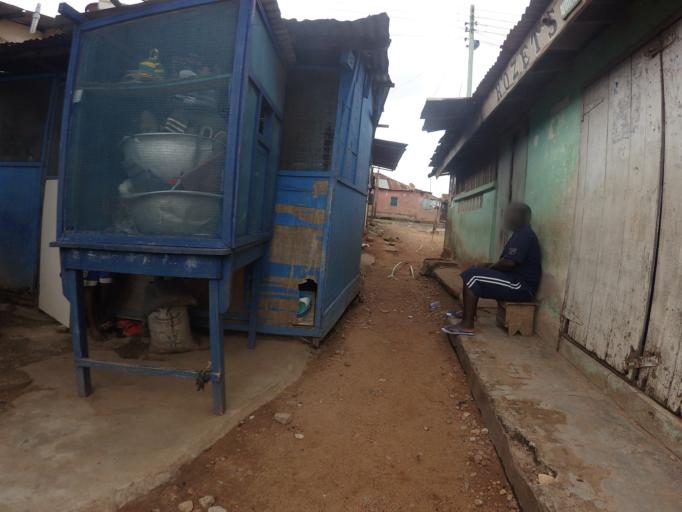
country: GH
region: Greater Accra
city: Accra
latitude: 5.5871
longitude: -0.2020
